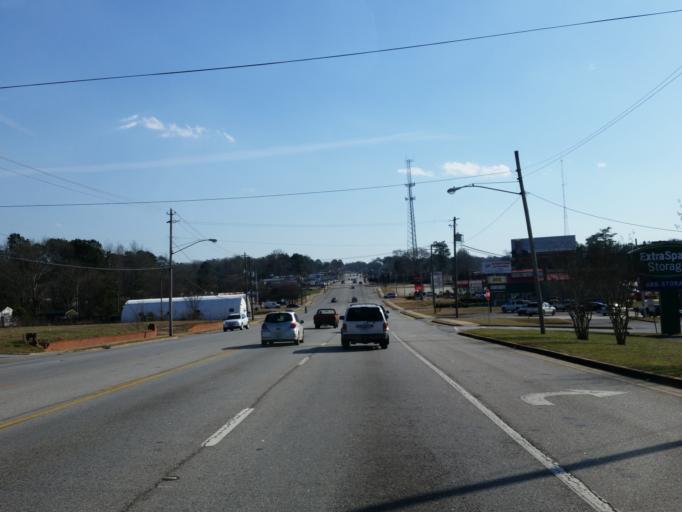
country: US
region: Georgia
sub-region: Spalding County
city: Experiment
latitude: 33.2594
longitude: -84.2887
